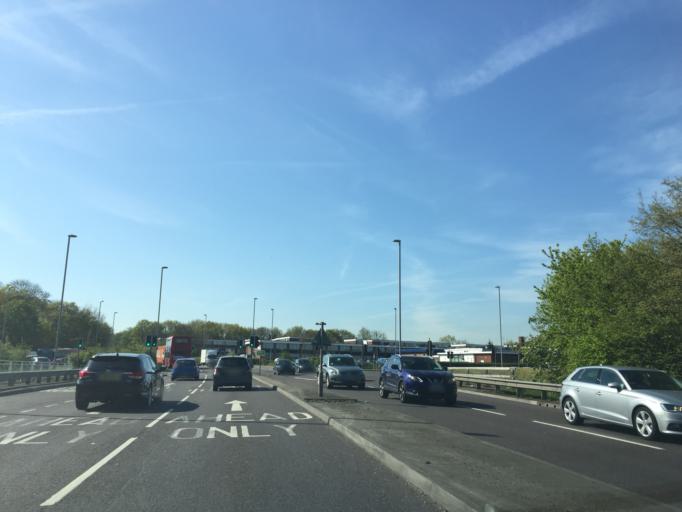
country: GB
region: England
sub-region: Essex
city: Harlow
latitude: 51.7572
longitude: 0.1272
